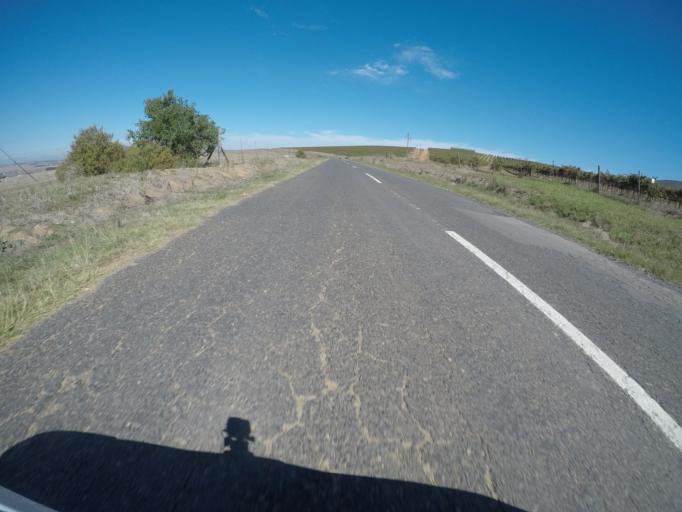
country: ZA
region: Western Cape
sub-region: City of Cape Town
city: Sunset Beach
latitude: -33.7105
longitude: 18.5827
